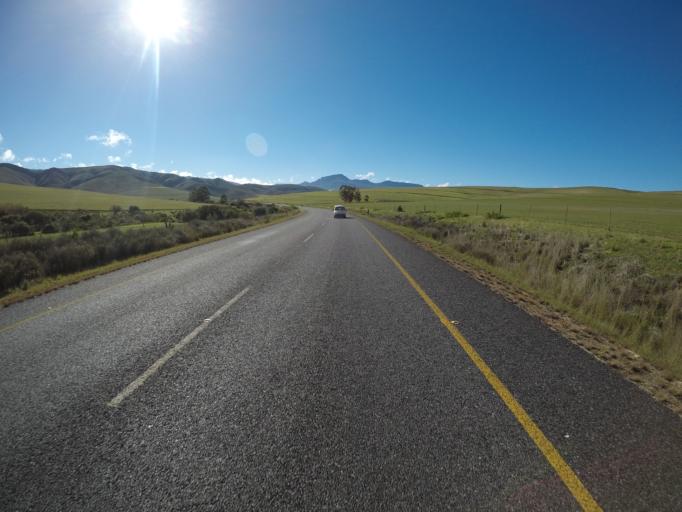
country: ZA
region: Western Cape
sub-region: Overberg District Municipality
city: Caledon
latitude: -34.1111
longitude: 19.5248
